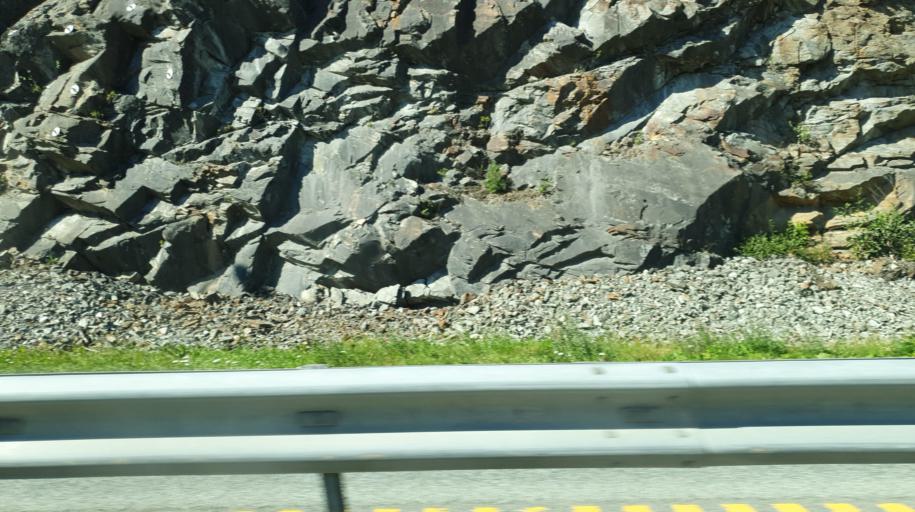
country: NO
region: Nord-Trondelag
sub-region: Levanger
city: Levanger
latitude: 63.7363
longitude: 11.3234
